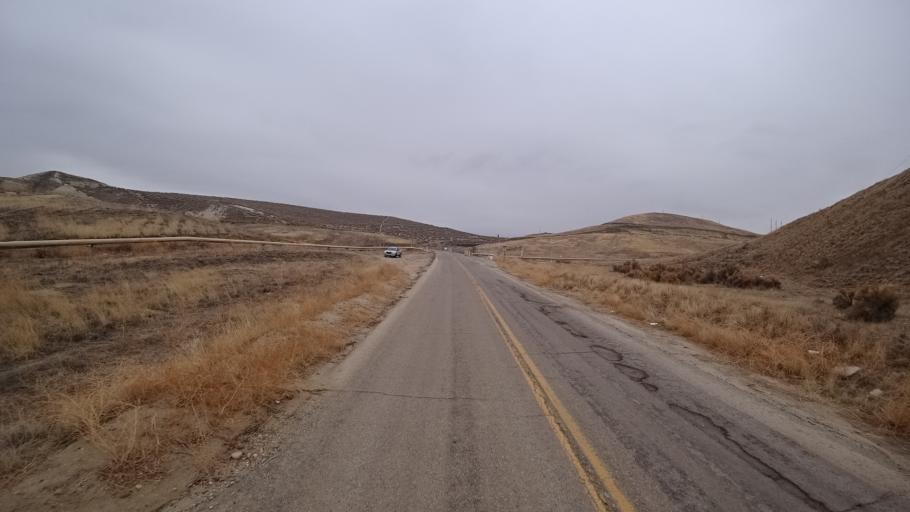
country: US
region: California
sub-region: Kern County
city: Oildale
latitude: 35.4232
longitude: -118.9353
